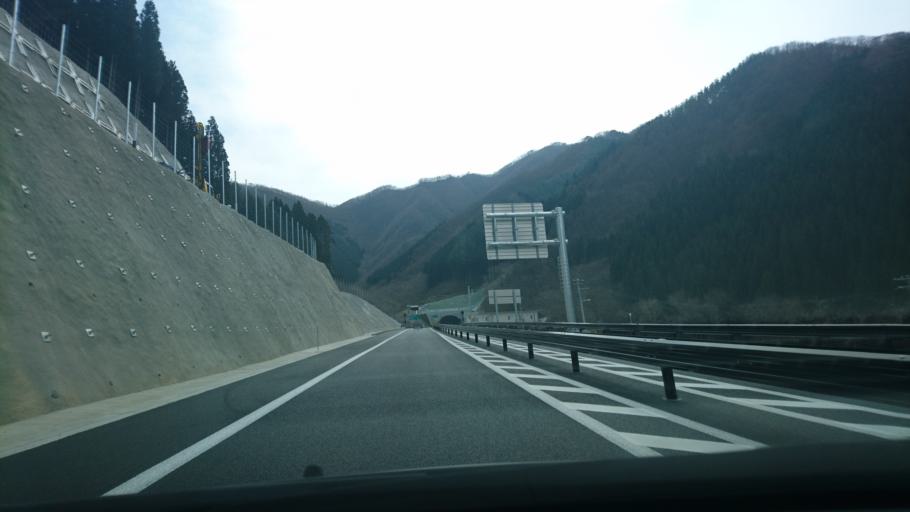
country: JP
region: Iwate
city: Kamaishi
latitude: 39.2449
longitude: 141.8434
